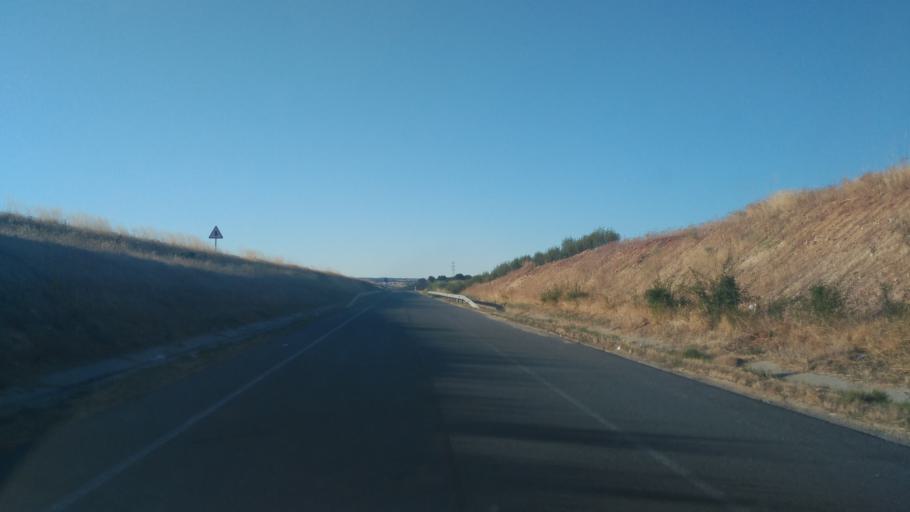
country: ES
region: Castille and Leon
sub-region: Provincia de Salamanca
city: Montejo
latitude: 40.6703
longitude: -5.6179
